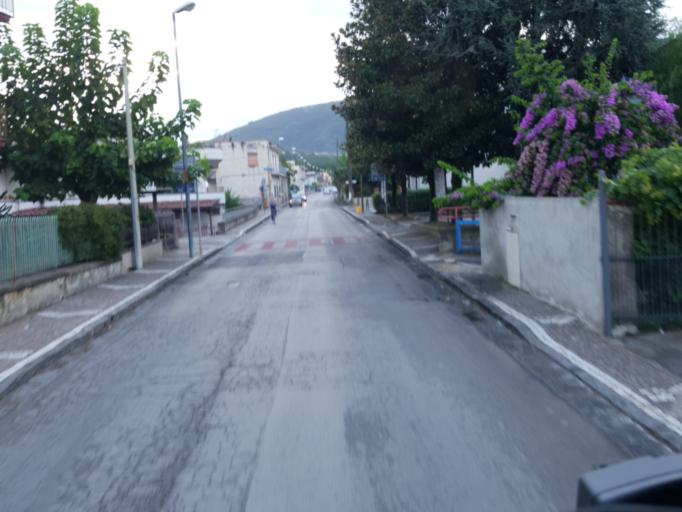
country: IT
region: Campania
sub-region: Provincia di Napoli
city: Palma Campania
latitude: 40.8795
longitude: 14.5541
